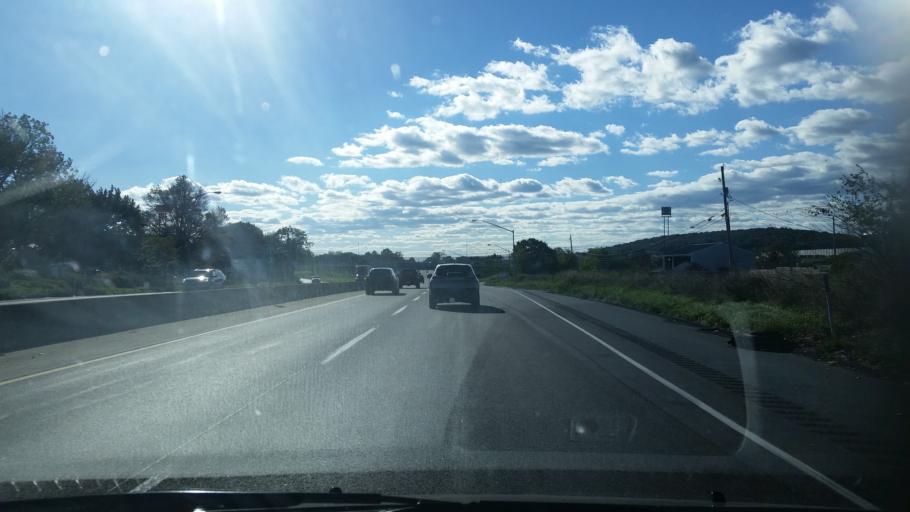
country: US
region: Pennsylvania
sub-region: Lebanon County
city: Myerstown
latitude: 40.4775
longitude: -76.2907
